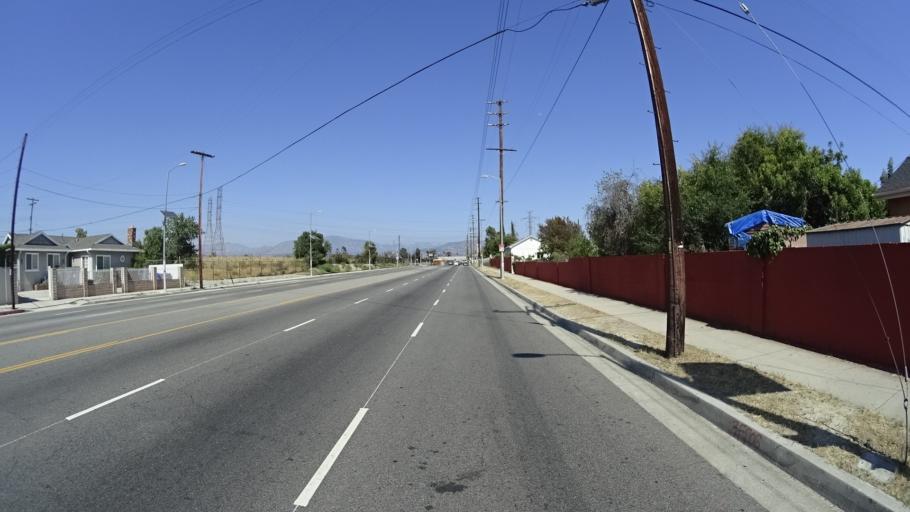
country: US
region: California
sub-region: Los Angeles County
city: Van Nuys
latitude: 34.2216
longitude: -118.4170
